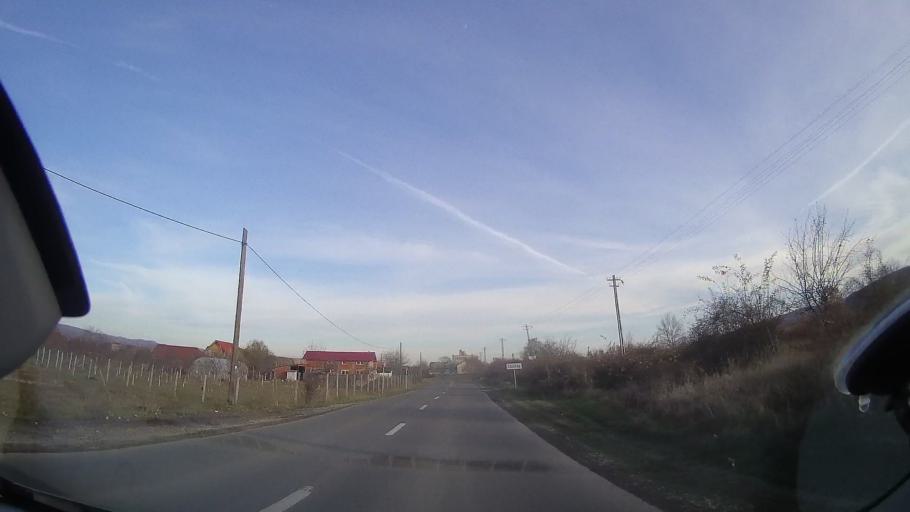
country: RO
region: Bihor
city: Lugasu de Jos
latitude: 47.0405
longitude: 22.3511
